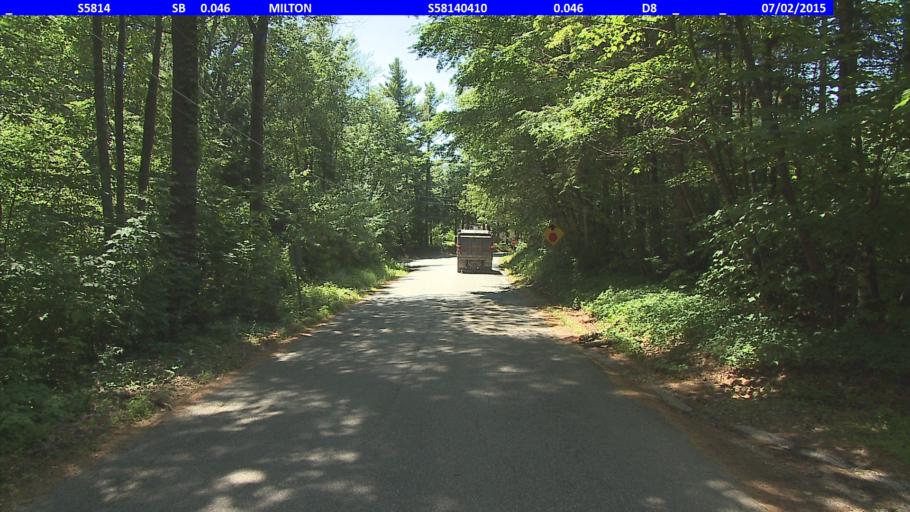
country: US
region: Vermont
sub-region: Chittenden County
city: Milton
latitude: 44.6319
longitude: -73.1797
